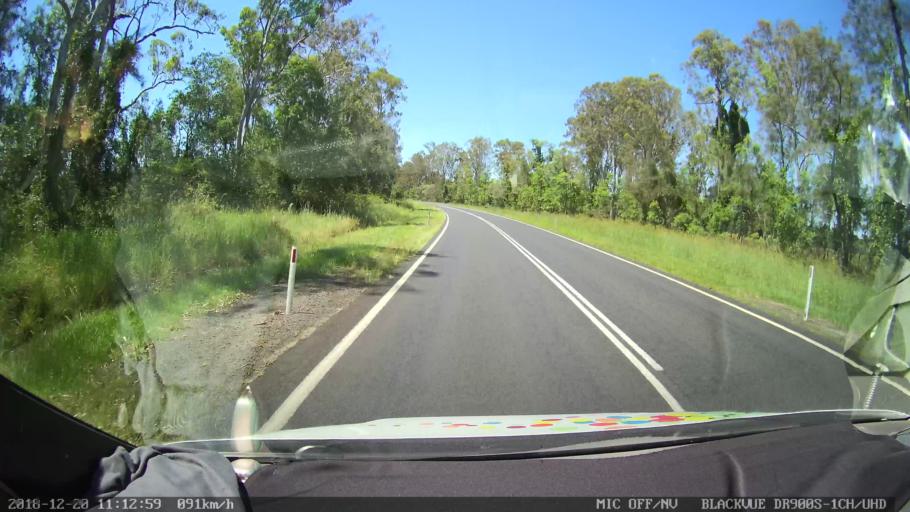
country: AU
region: New South Wales
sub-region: Richmond Valley
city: Casino
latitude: -28.9816
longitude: 153.0094
